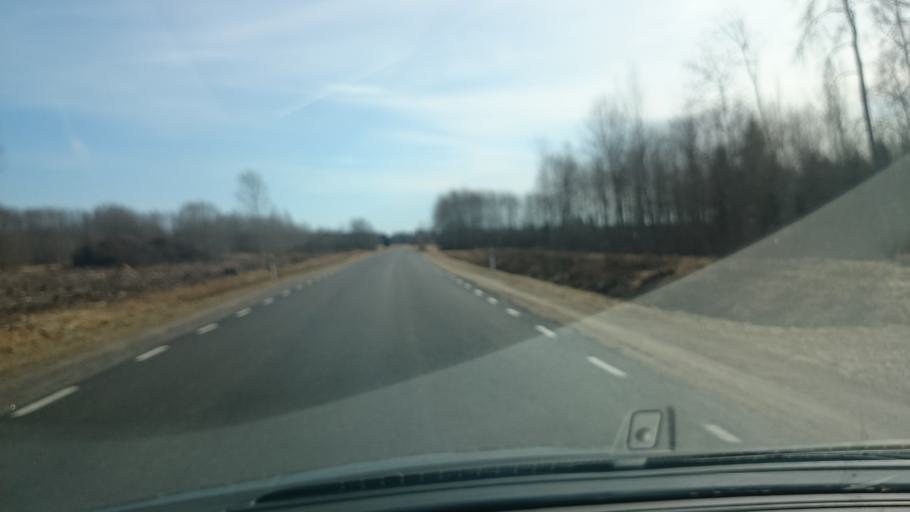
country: EE
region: Paernumaa
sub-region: Tootsi vald
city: Tootsi
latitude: 58.6396
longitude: 24.9047
